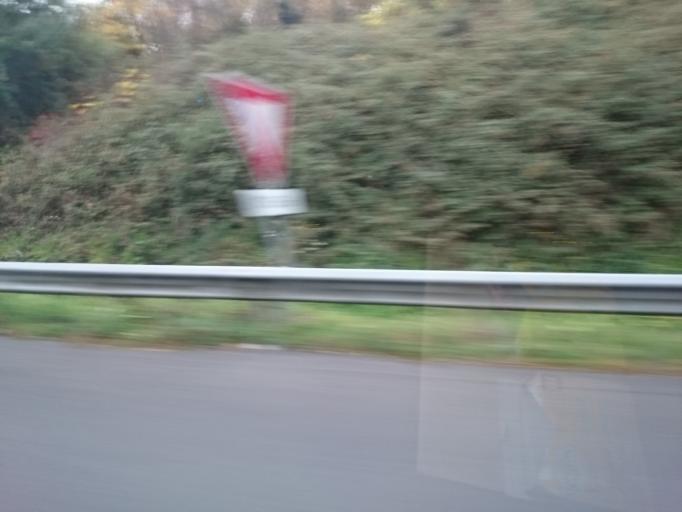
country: FR
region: Pays de la Loire
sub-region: Departement de la Loire-Atlantique
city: Orvault
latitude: 47.2655
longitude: -1.5851
